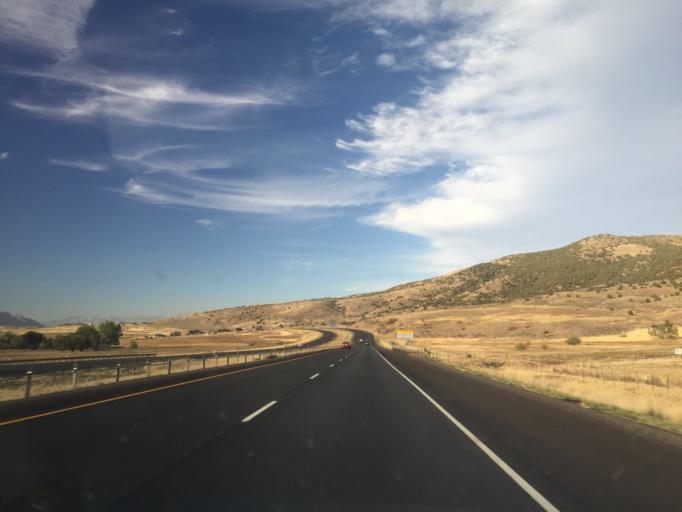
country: US
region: Utah
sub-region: Utah County
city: Santaquin
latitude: 39.9157
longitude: -111.8162
